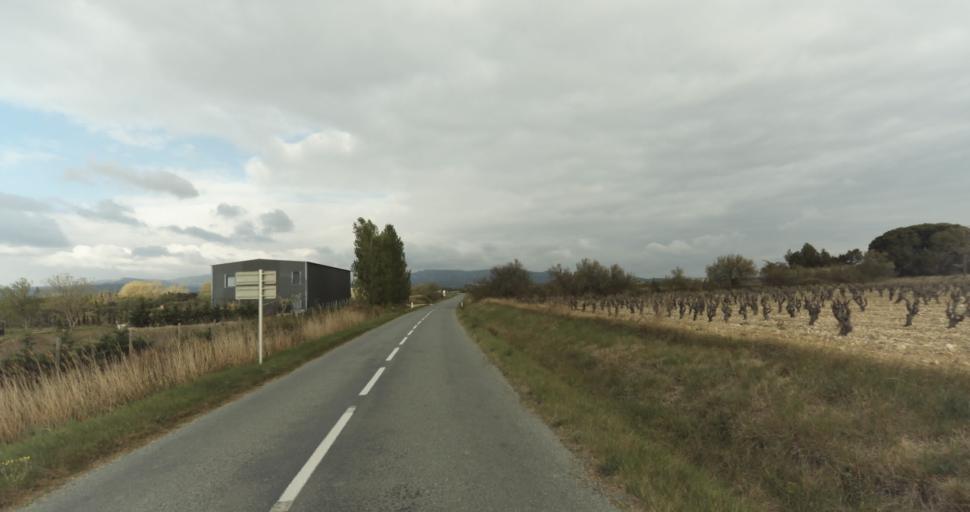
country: FR
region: Languedoc-Roussillon
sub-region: Departement de l'Aude
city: Leucate
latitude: 42.9297
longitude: 3.0040
